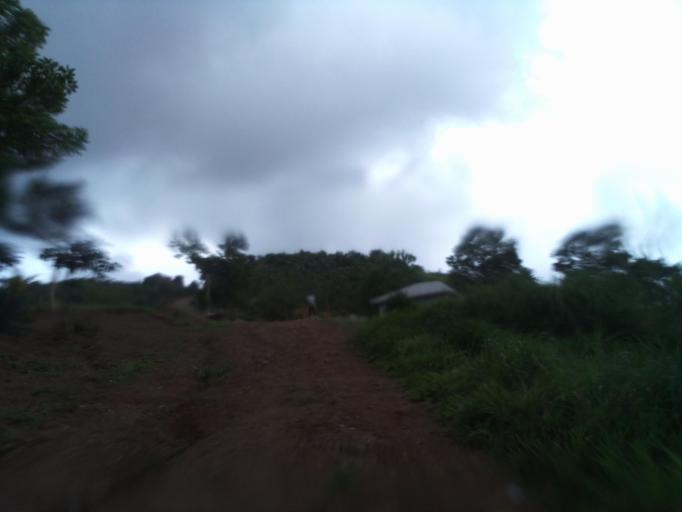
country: SL
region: Eastern Province
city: Kenema
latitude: 7.8508
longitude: -11.1868
